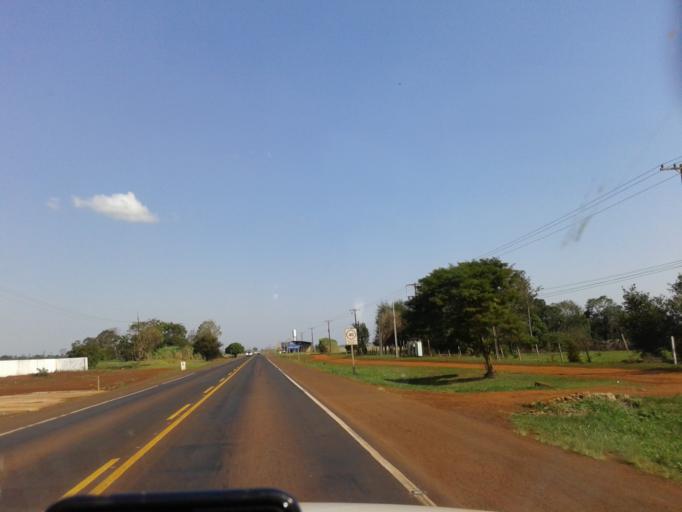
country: PY
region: Alto Parana
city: Santa Rita
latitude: -25.6851
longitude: -55.0091
